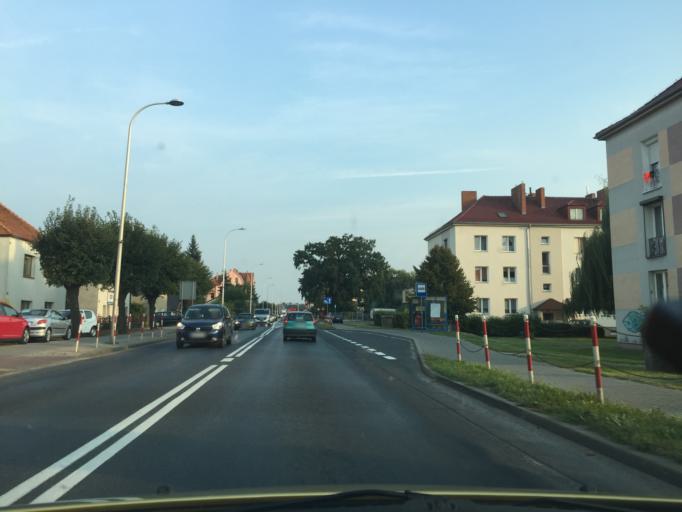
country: PL
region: Greater Poland Voivodeship
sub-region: Powiat jarocinski
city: Jarocin
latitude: 51.9649
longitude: 17.5089
